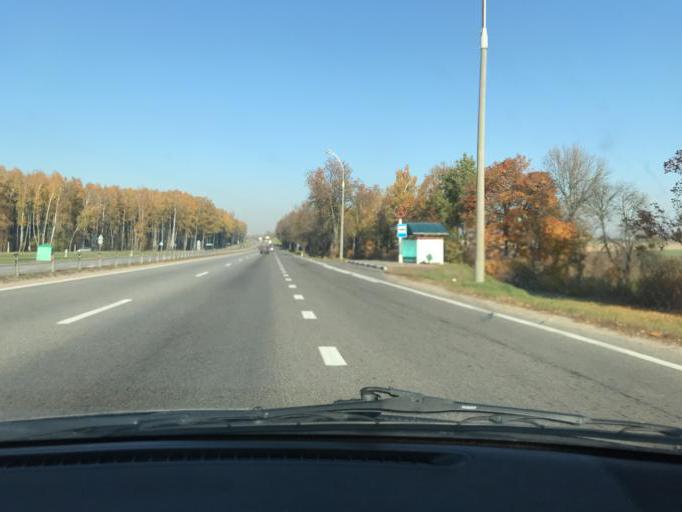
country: BY
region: Minsk
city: Samakhvalavichy
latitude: 53.7578
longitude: 27.5170
